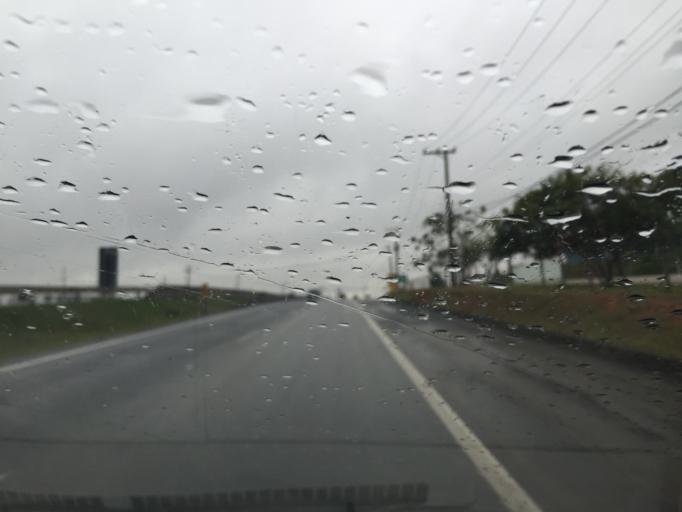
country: BR
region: Sao Paulo
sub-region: Itu
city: Itu
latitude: -23.2529
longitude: -47.3267
